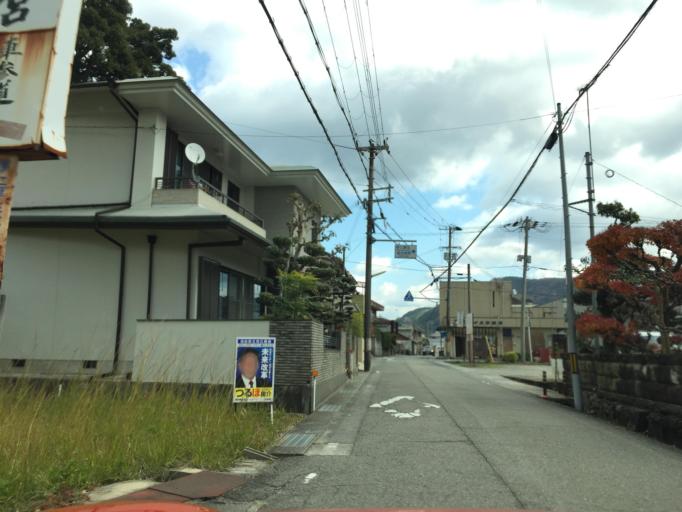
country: JP
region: Wakayama
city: Iwade
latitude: 34.1649
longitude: 135.2943
